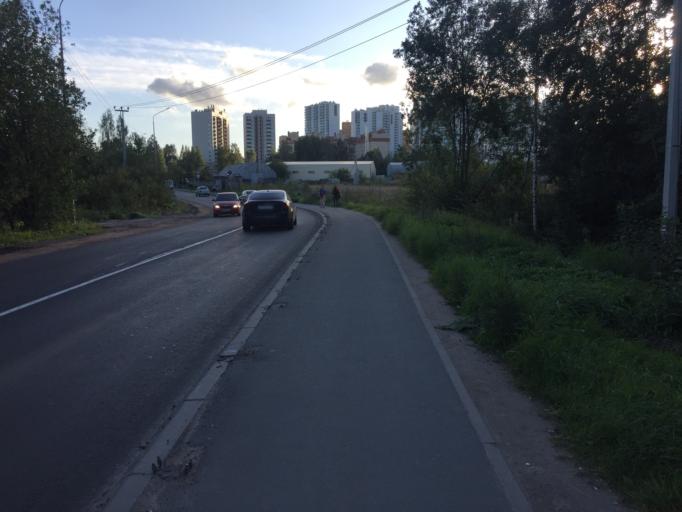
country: RU
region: Leningrad
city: Murino
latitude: 60.0560
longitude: 30.4587
